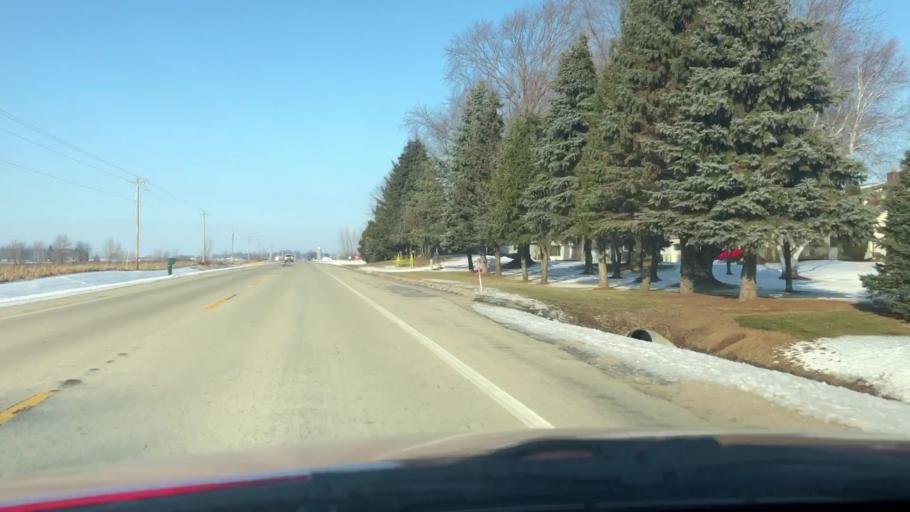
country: US
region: Wisconsin
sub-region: Outagamie County
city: Seymour
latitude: 44.4764
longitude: -88.3296
